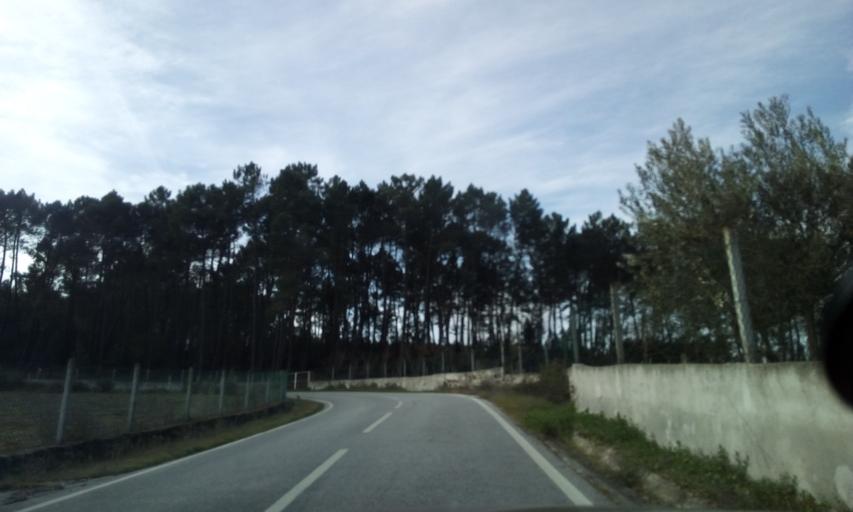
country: PT
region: Guarda
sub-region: Fornos de Algodres
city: Fornos de Algodres
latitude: 40.7000
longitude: -7.5614
